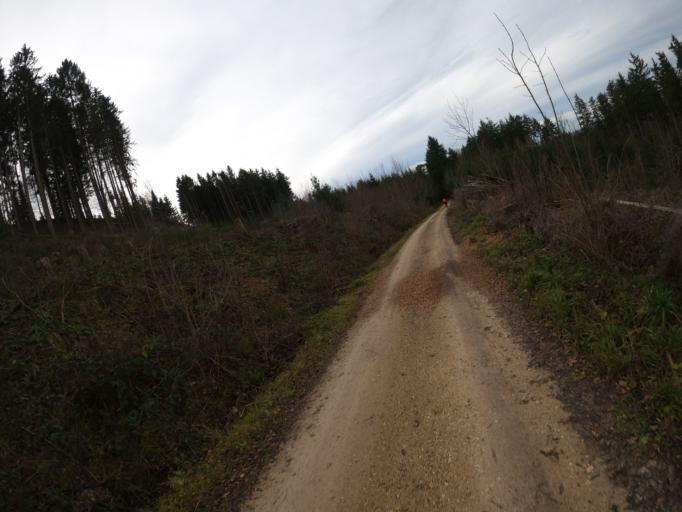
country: DE
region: Baden-Wuerttemberg
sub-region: Regierungsbezirk Stuttgart
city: Ottenbach
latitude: 48.7560
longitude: 9.7652
